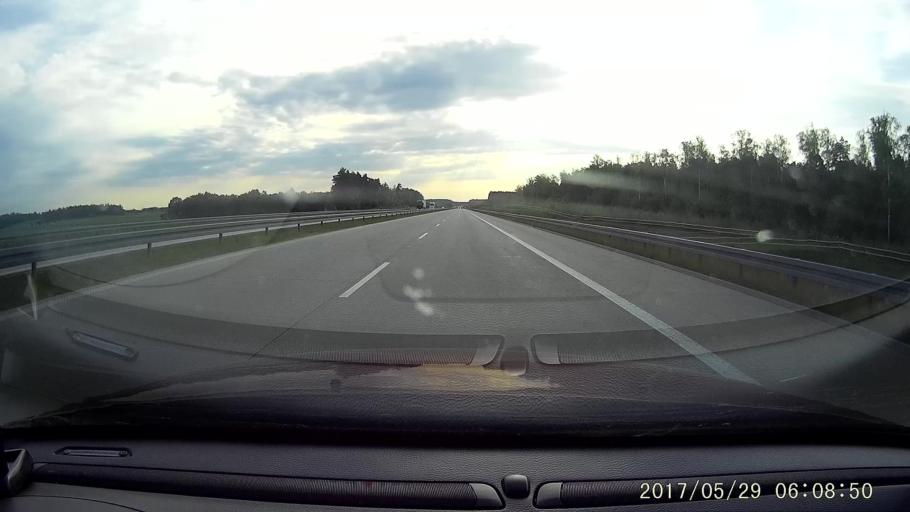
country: PL
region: Lower Silesian Voivodeship
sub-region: Powiat lubanski
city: Siekierczyn
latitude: 51.2055
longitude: 15.1614
